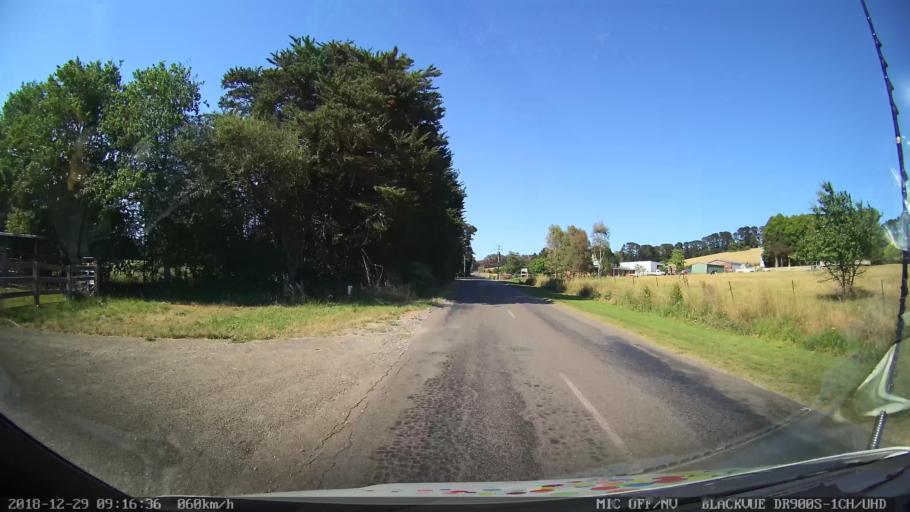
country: AU
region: New South Wales
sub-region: Upper Lachlan Shire
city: Crookwell
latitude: -34.4598
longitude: 149.4506
